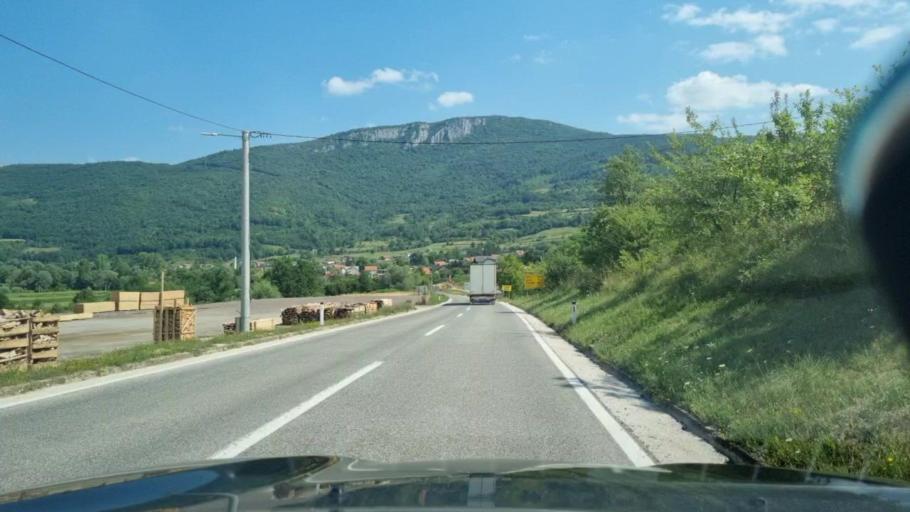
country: BA
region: Federation of Bosnia and Herzegovina
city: Kljuc
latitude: 44.4987
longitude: 16.8191
